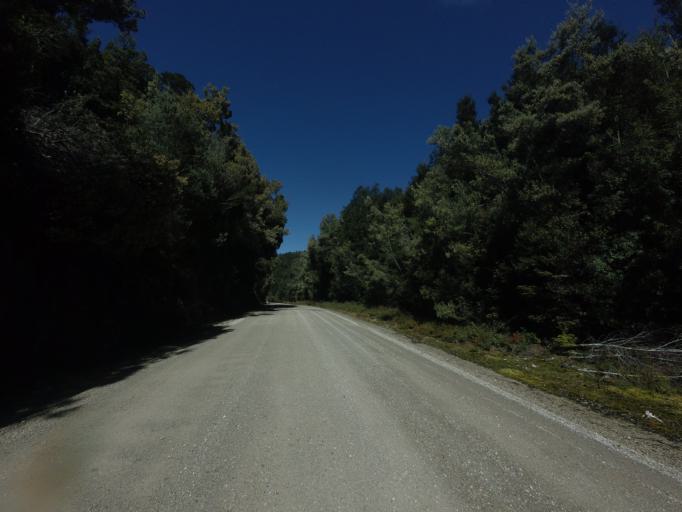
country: AU
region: Tasmania
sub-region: Huon Valley
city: Geeveston
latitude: -42.8365
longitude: 146.3783
